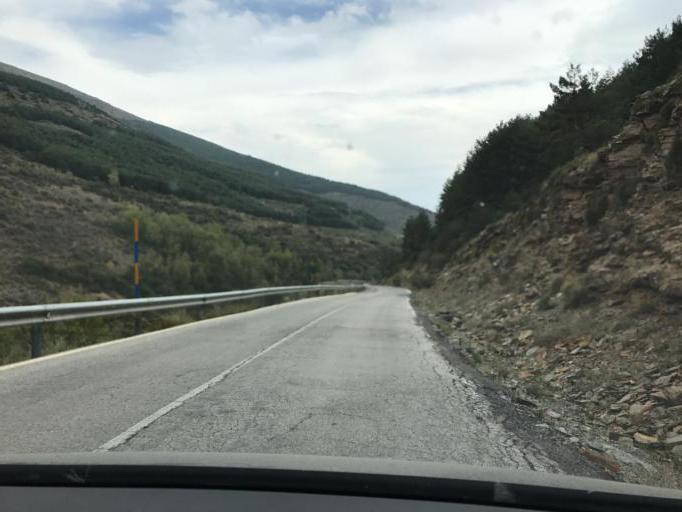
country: ES
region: Andalusia
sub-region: Provincia de Almeria
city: Bayarcal
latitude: 37.0887
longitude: -3.0261
